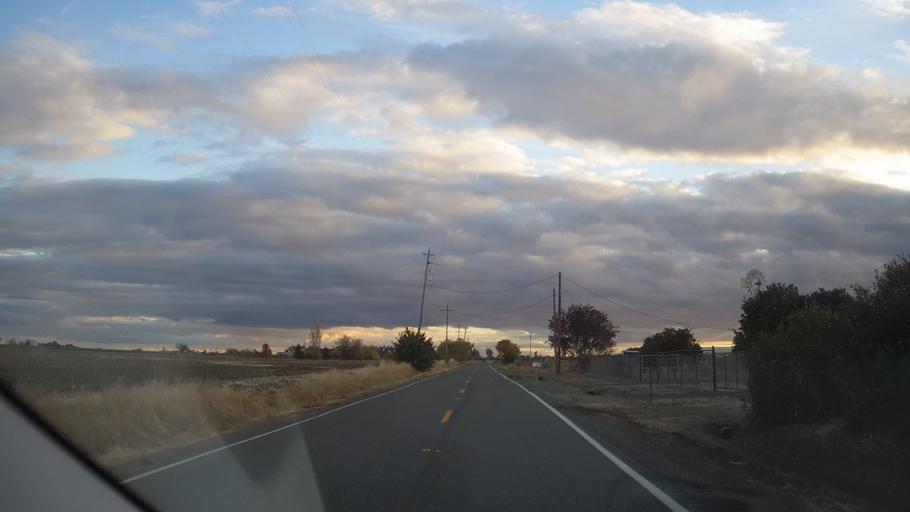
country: US
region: California
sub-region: Solano County
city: Hartley
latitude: 38.3980
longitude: -121.9059
